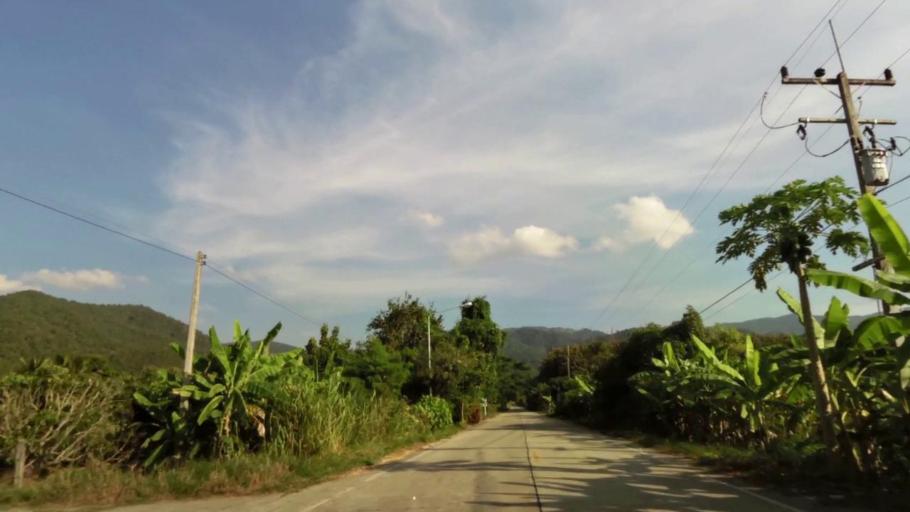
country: TH
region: Chiang Rai
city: Khun Tan
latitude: 19.8828
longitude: 100.2958
